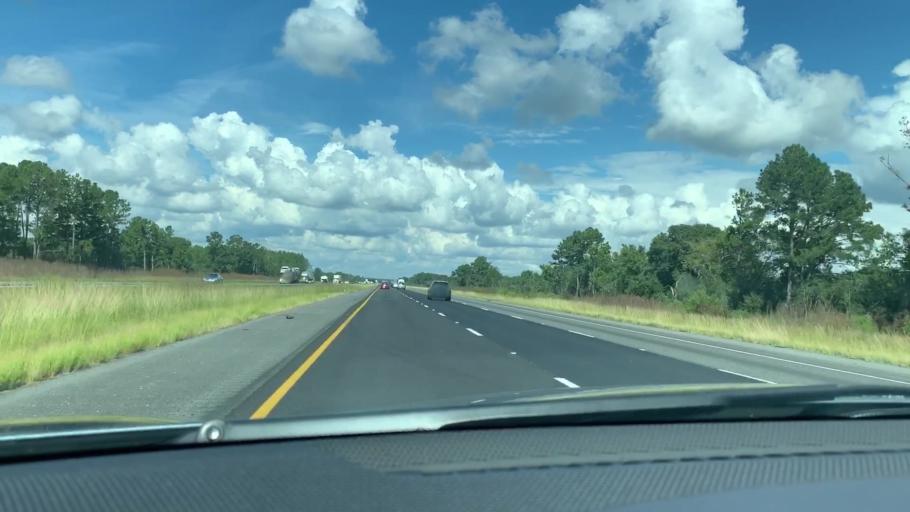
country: US
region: Georgia
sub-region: Camden County
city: Woodbine
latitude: 31.0059
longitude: -81.6617
